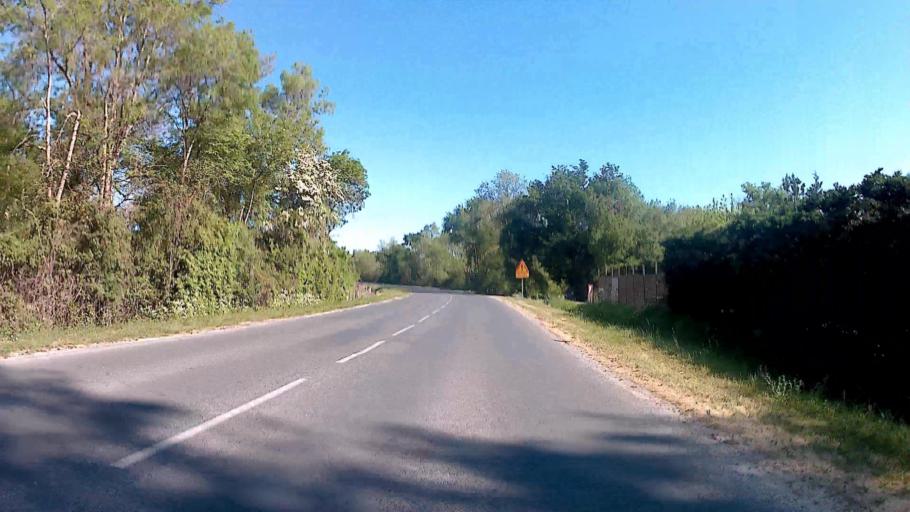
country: FR
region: Aquitaine
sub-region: Departement de la Gironde
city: Cadaujac
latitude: 44.7595
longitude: -0.5287
